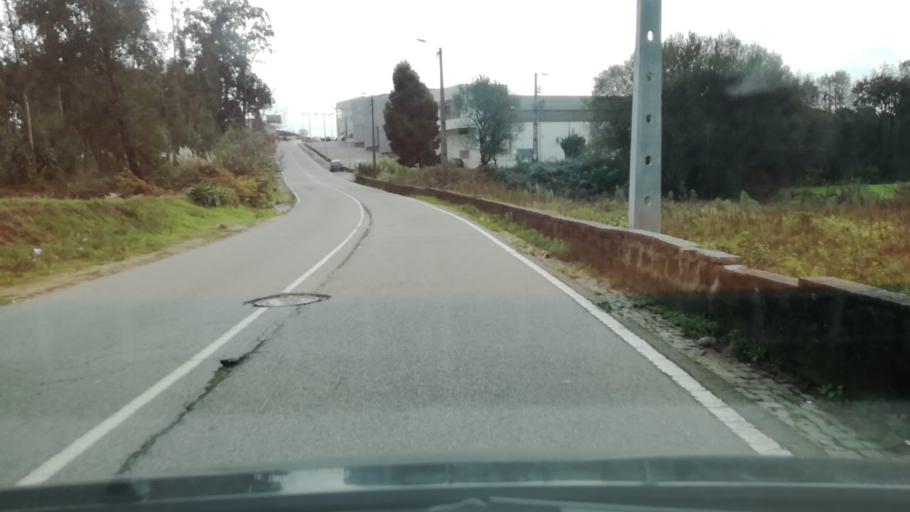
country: PT
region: Porto
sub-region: Maia
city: Maia
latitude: 41.2439
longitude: -8.6359
